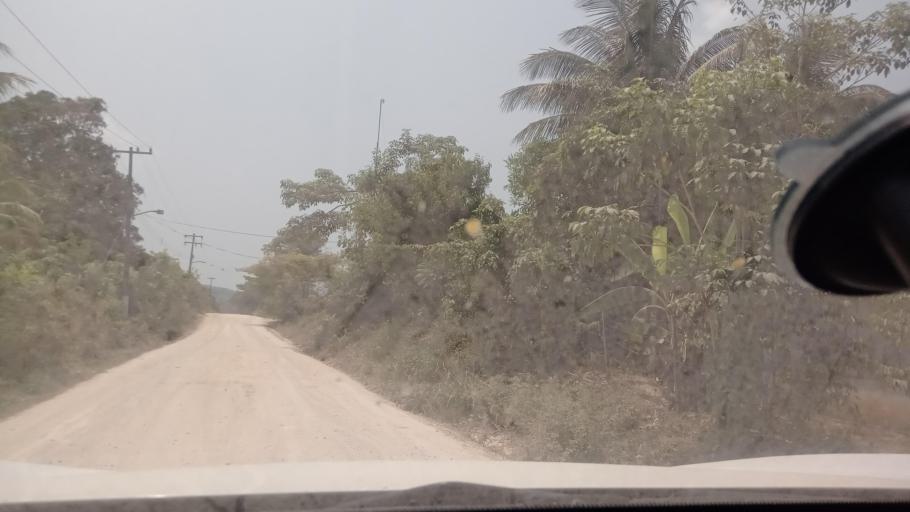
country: MX
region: Chiapas
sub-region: Tecpatan
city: Raudales Malpaso
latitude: 17.4742
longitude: -93.8170
